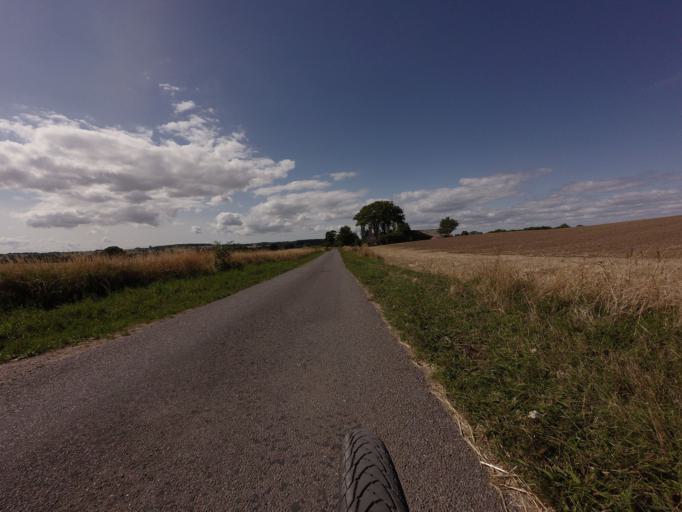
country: DK
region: Zealand
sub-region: Vordingborg Kommune
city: Stege
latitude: 55.0199
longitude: 12.4563
